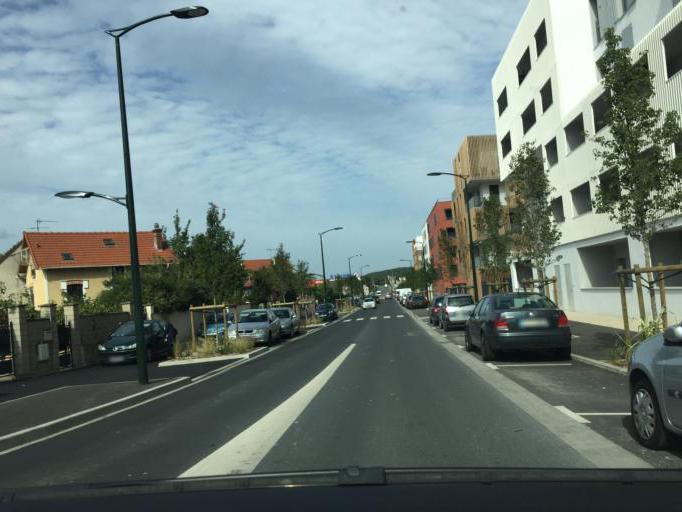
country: FR
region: Ile-de-France
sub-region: Departement de l'Essonne
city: Palaiseau
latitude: 48.7245
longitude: 2.2471
